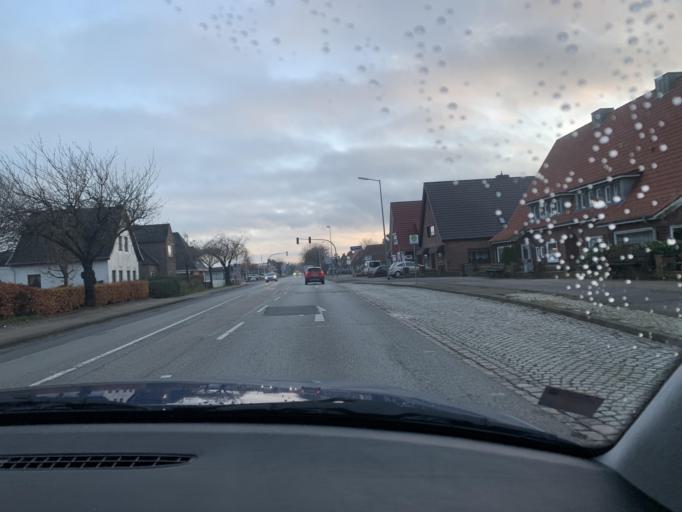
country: DE
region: Schleswig-Holstein
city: Heide
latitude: 54.1872
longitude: 9.0901
